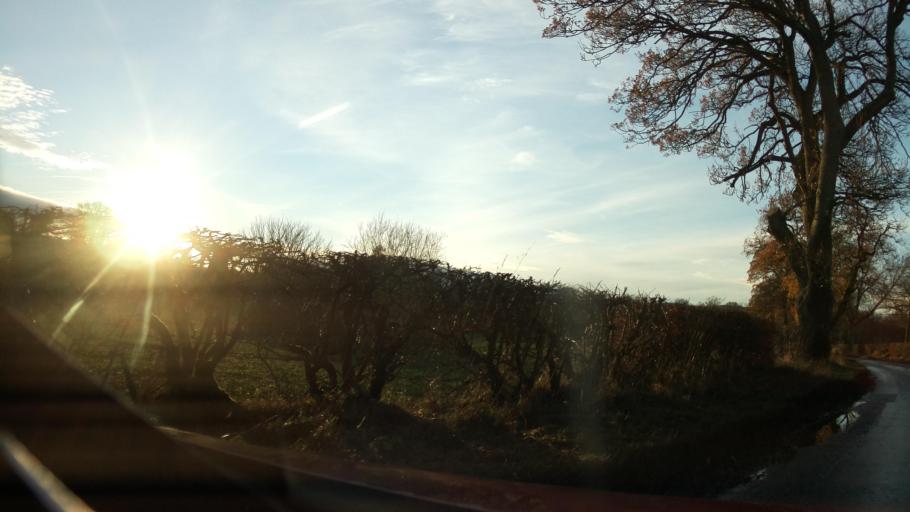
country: GB
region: Scotland
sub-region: Angus
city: Forfar
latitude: 56.5881
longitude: -2.8779
